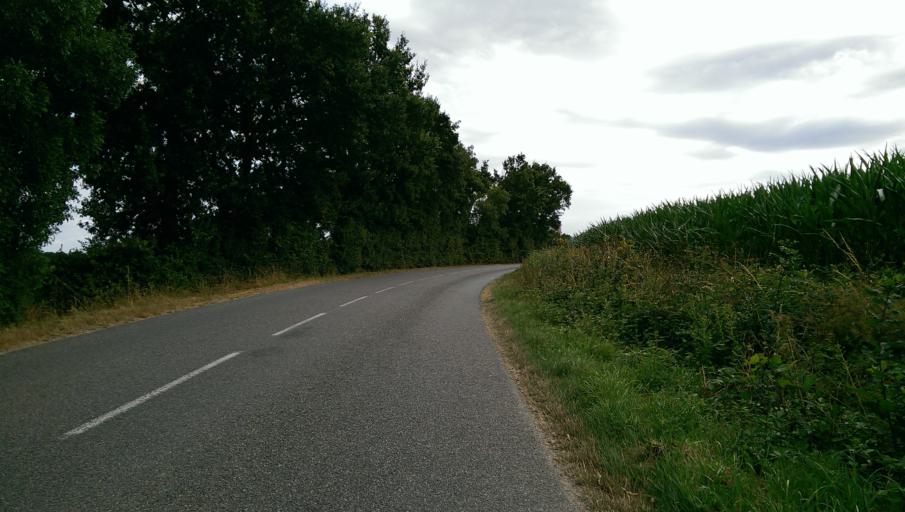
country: FR
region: Pays de la Loire
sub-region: Departement de la Loire-Atlantique
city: Vieillevigne
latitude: 46.9782
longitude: -1.4306
